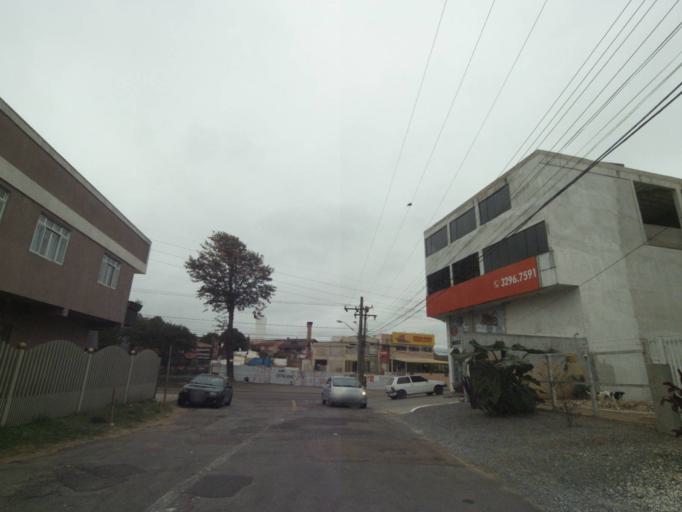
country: BR
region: Parana
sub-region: Pinhais
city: Pinhais
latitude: -25.4728
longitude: -49.2367
